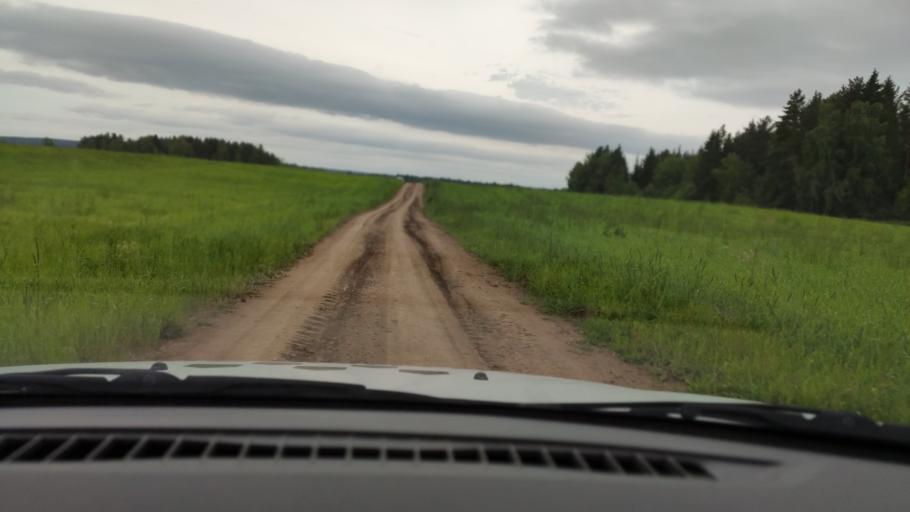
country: RU
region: Perm
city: Orda
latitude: 57.2979
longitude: 56.5928
